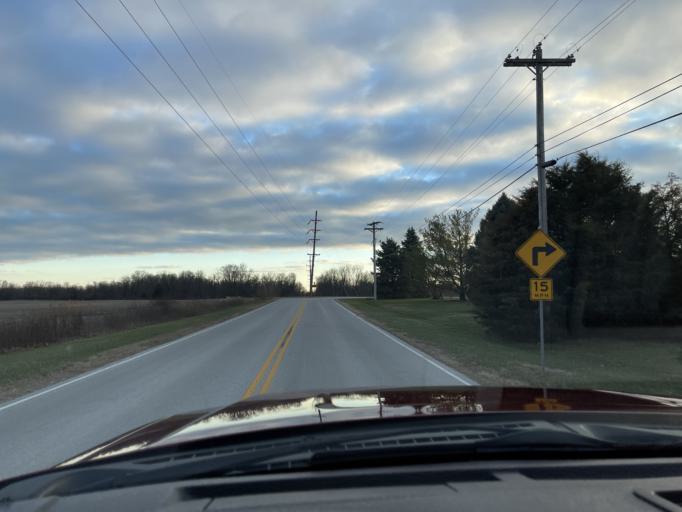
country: US
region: Indiana
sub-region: Hendricks County
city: Avon
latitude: 39.7733
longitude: -86.4287
